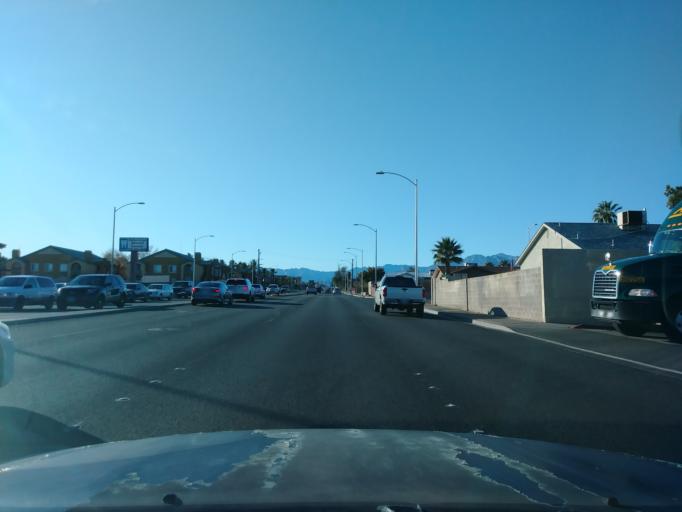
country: US
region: Nevada
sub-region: Clark County
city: Spring Valley
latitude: 36.1592
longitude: -115.2458
